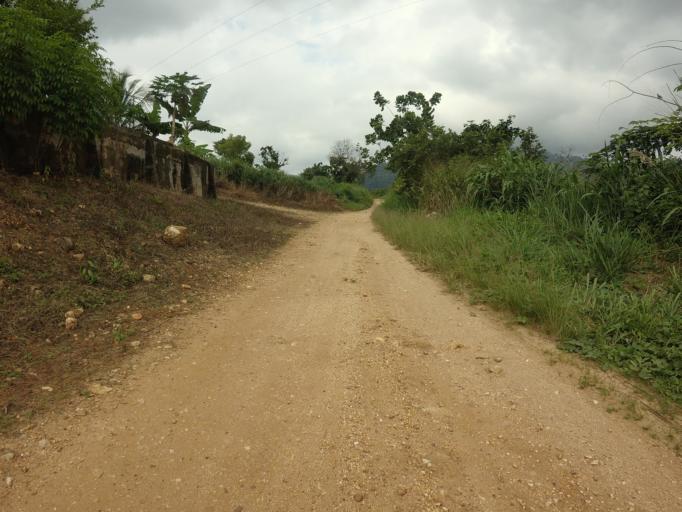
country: TG
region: Plateaux
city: Kpalime
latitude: 6.8660
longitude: 0.4418
